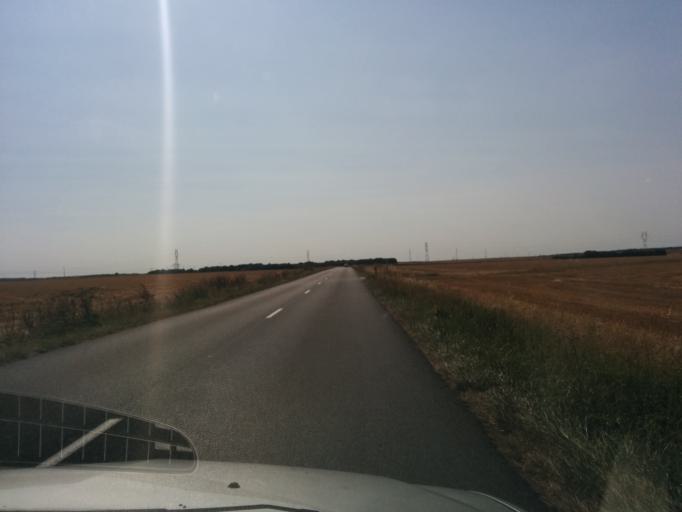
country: FR
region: Poitou-Charentes
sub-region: Departement de la Vienne
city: Moncontour
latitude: 46.8111
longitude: -0.0553
